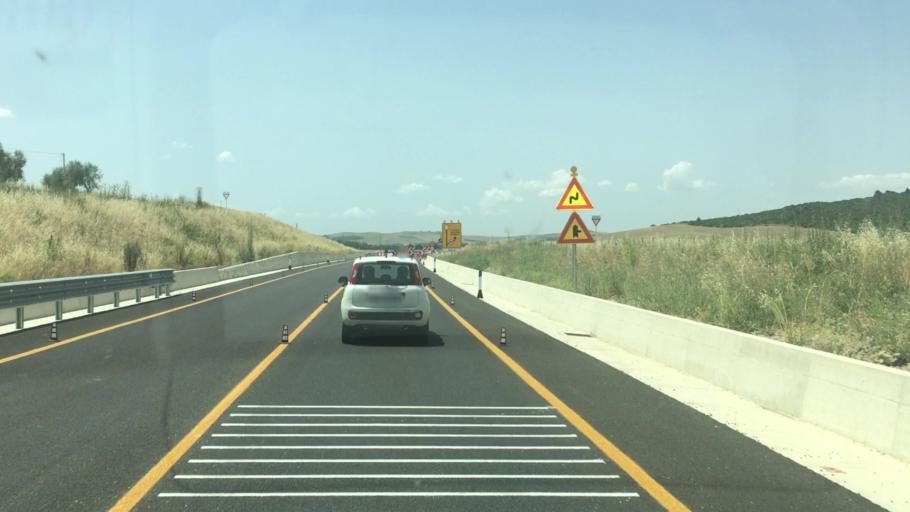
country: IT
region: Basilicate
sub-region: Provincia di Matera
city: La Martella
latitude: 40.6714
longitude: 16.4965
